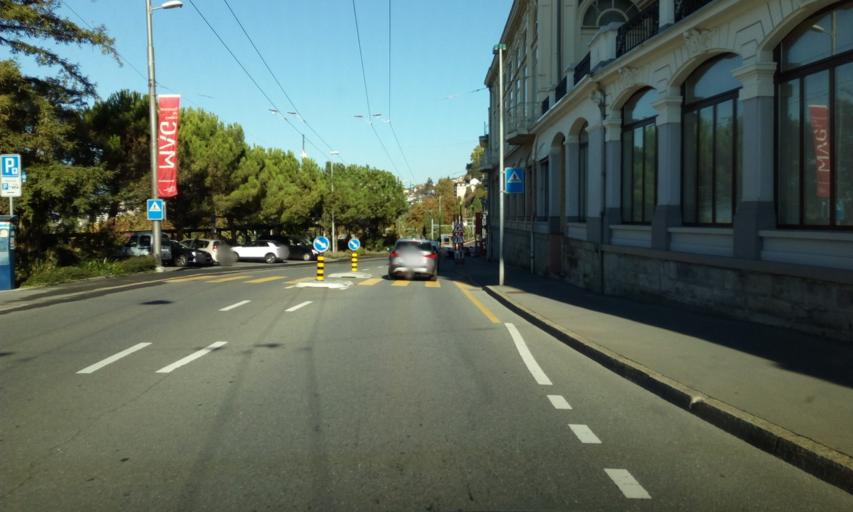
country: CH
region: Vaud
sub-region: Riviera-Pays-d'Enhaut District
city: Montreux
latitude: 46.4249
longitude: 6.9242
